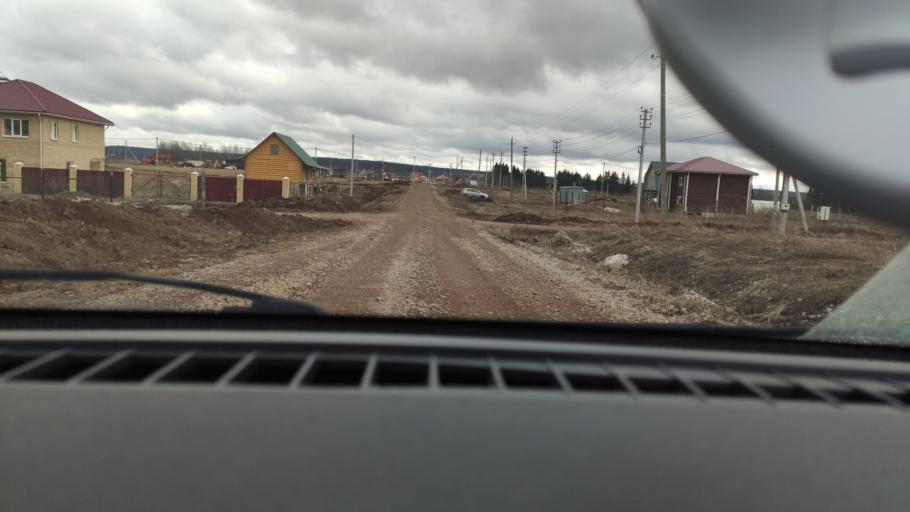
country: RU
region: Perm
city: Ferma
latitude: 57.9483
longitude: 56.3397
